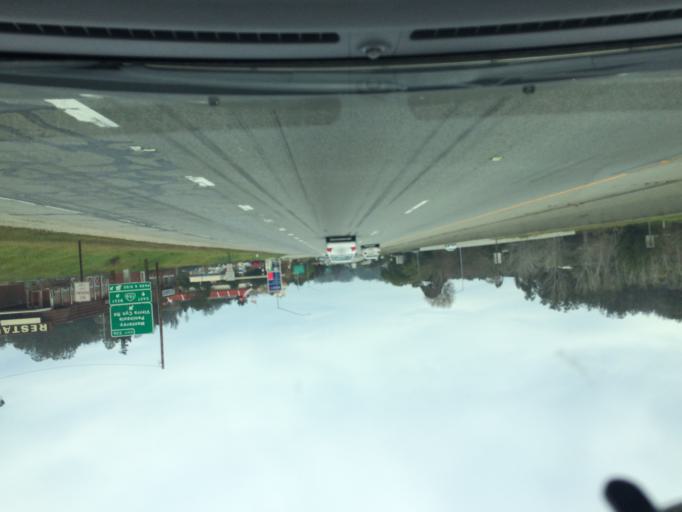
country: US
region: California
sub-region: Monterey County
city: Prunedale
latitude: 36.7905
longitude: -121.6673
